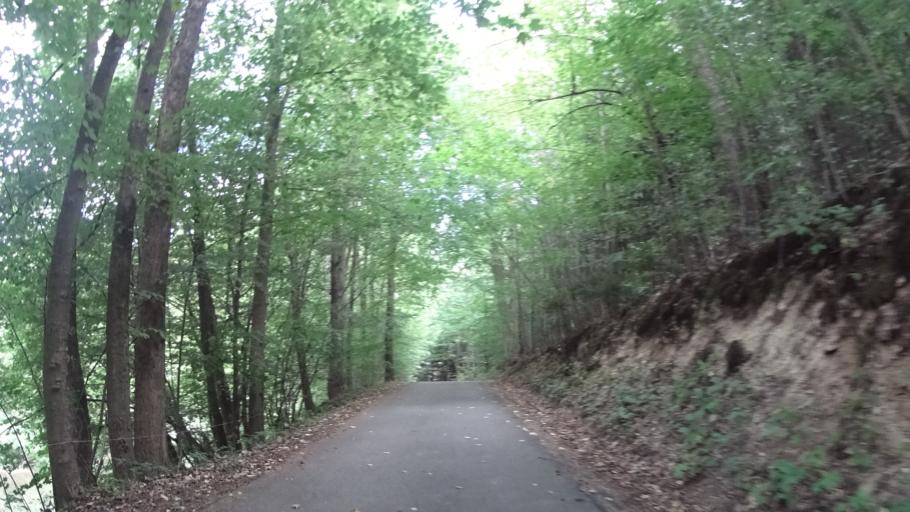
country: CZ
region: Pardubicky
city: Brandys nad Orlici
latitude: 49.9931
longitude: 16.3402
